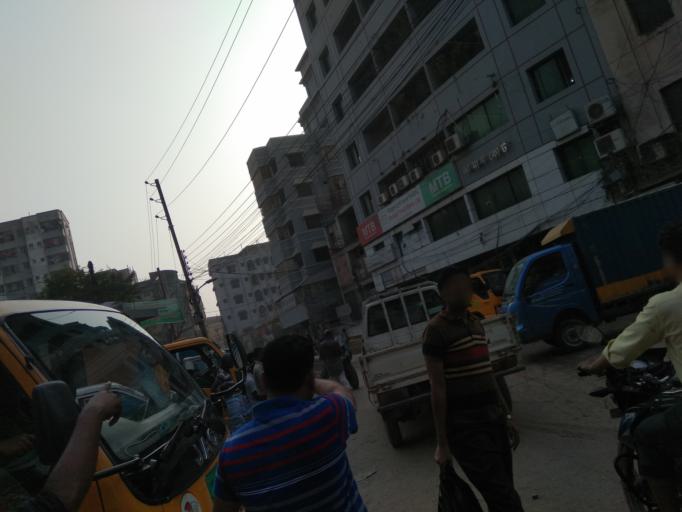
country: BD
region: Dhaka
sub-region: Dhaka
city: Dhaka
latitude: 23.7138
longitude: 90.4029
